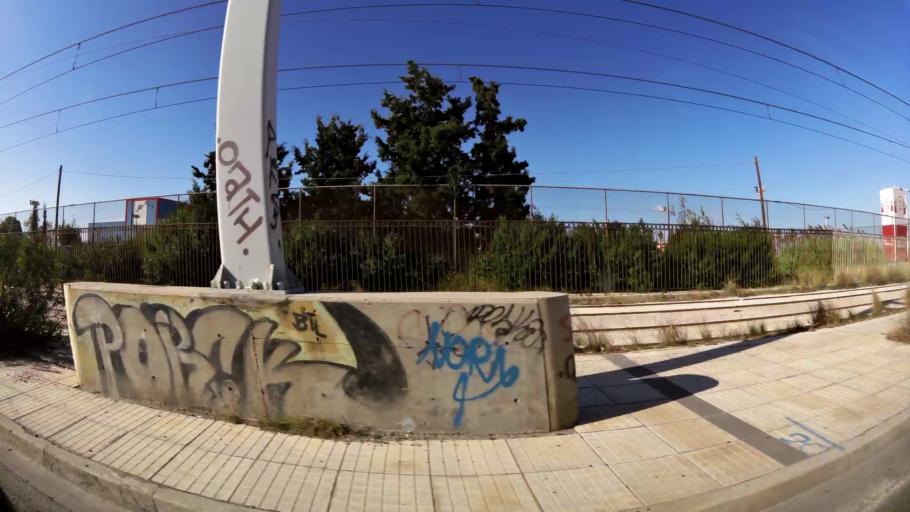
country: GR
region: Attica
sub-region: Nomarchia Athinas
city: Elliniko
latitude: 37.8882
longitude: 23.7250
